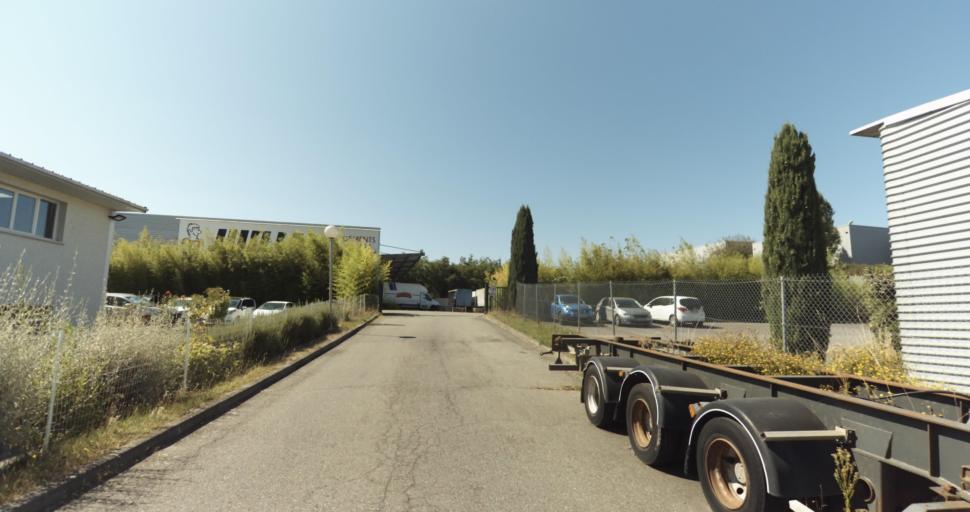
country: FR
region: Midi-Pyrenees
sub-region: Departement de la Haute-Garonne
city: Montrabe
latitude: 43.6410
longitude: 1.5012
